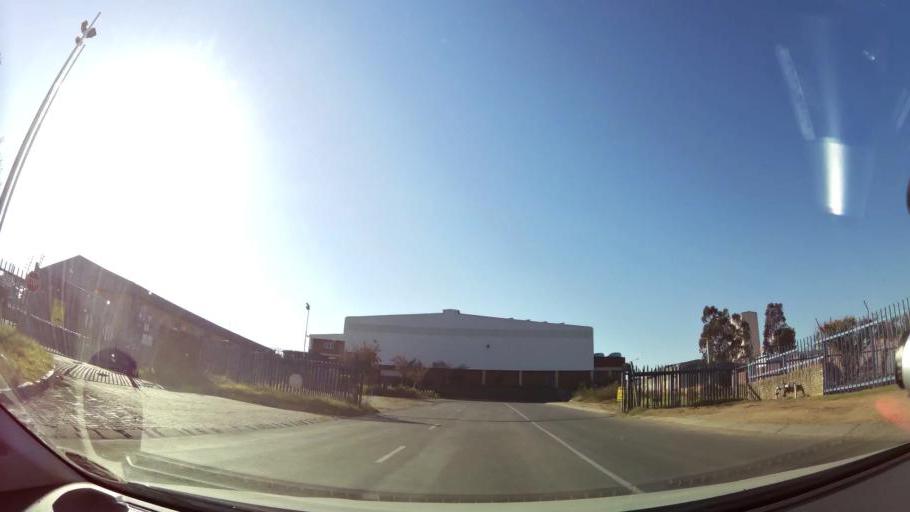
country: ZA
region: Gauteng
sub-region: City of Johannesburg Metropolitan Municipality
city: Modderfontein
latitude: -26.0611
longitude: 28.1750
